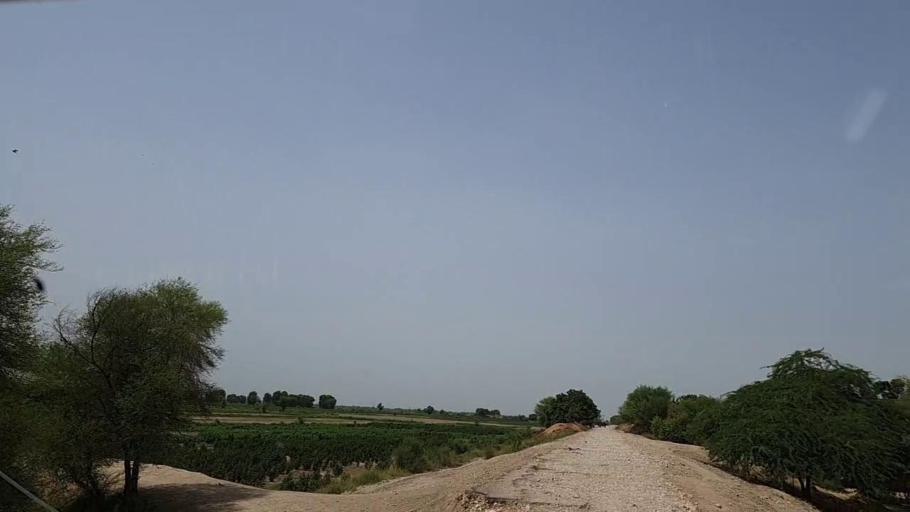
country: PK
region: Sindh
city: Tharu Shah
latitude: 27.0351
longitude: 68.1116
